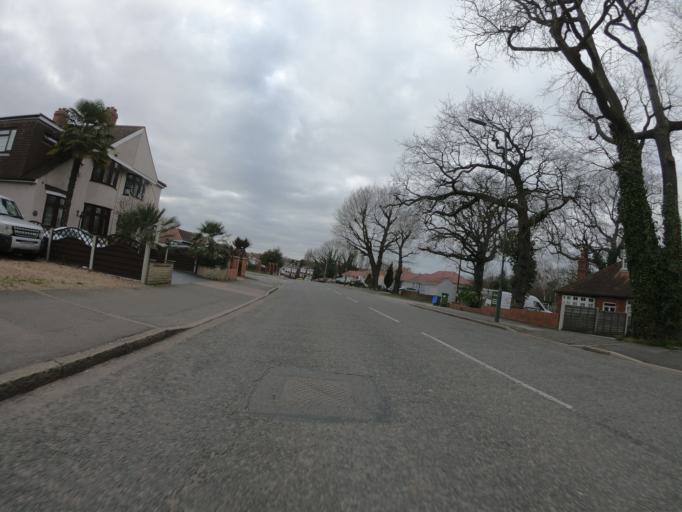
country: GB
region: England
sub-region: Greater London
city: Belvedere
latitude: 51.4787
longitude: 0.1600
